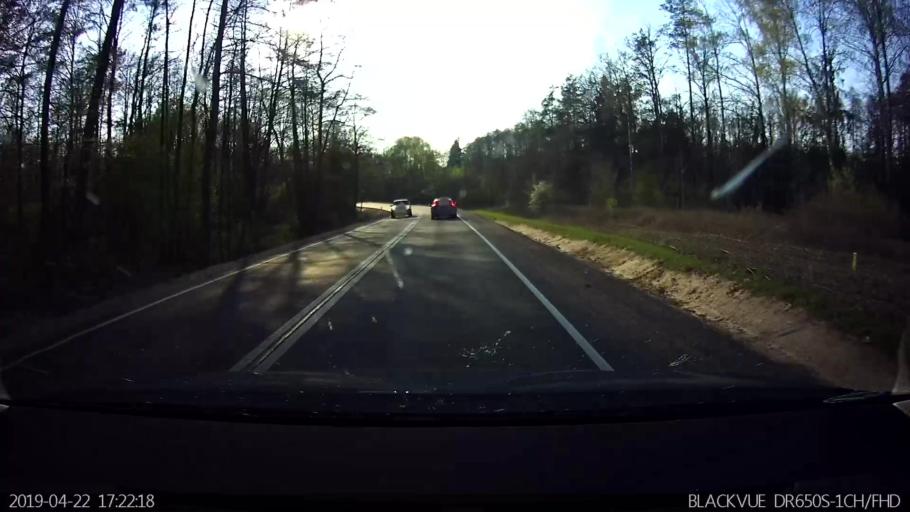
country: PL
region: Masovian Voivodeship
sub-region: Powiat sokolowski
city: Repki
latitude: 52.3910
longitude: 22.3418
